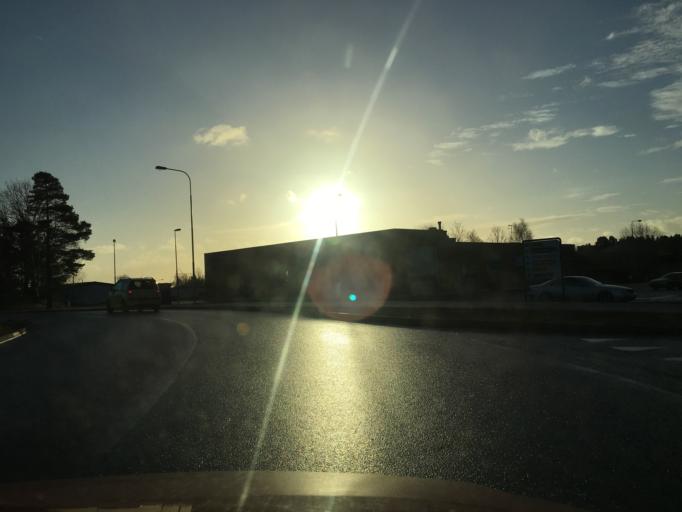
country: SE
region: Kalmar
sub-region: Vasterviks Kommun
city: Vaestervik
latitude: 57.7626
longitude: 16.6049
